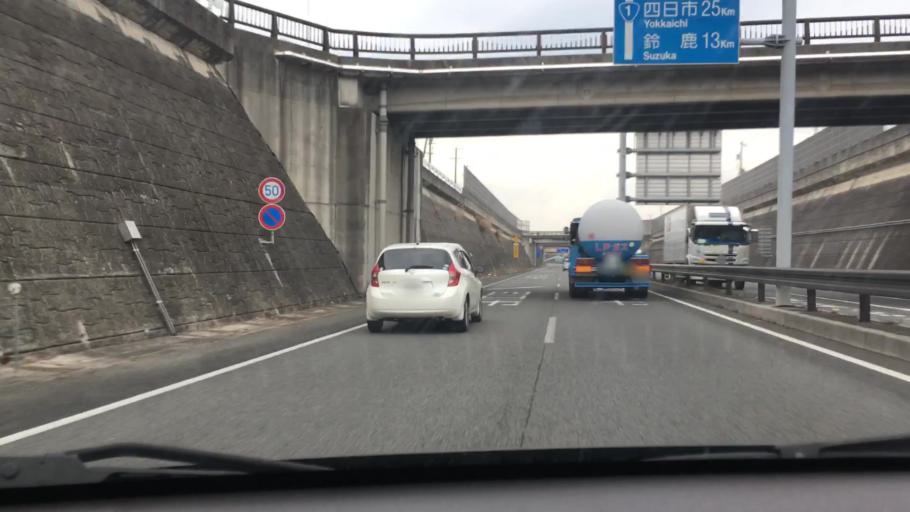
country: JP
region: Mie
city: Kameyama
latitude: 34.8593
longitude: 136.4261
